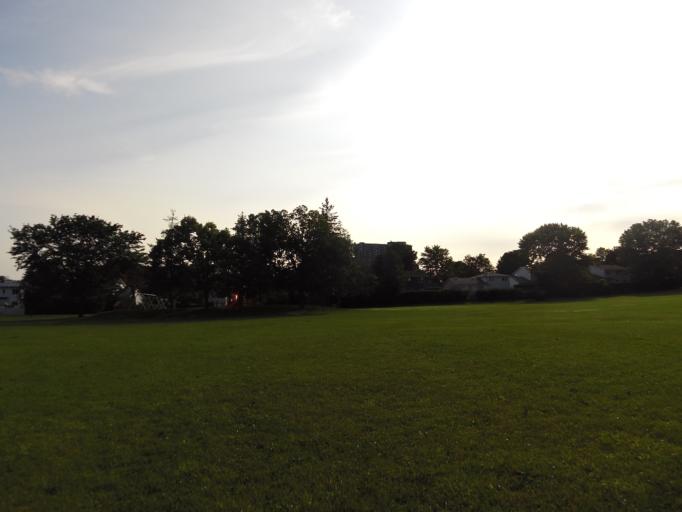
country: CA
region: Ontario
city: Bells Corners
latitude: 45.3677
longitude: -75.7919
